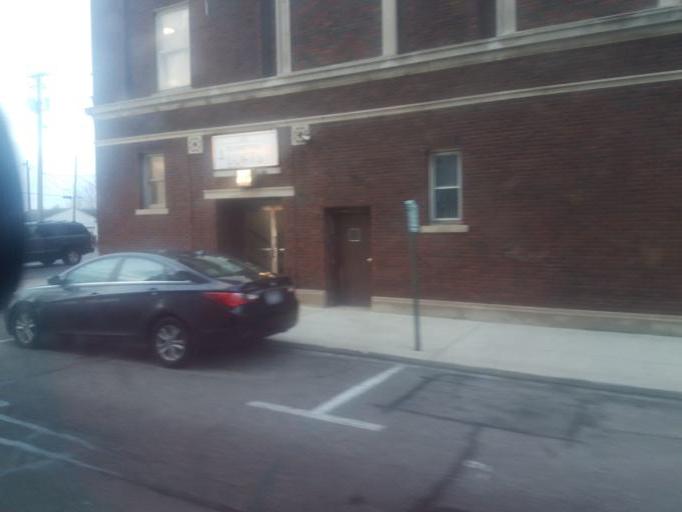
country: US
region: Ohio
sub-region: Marion County
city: Marion
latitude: 40.5882
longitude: -83.1337
